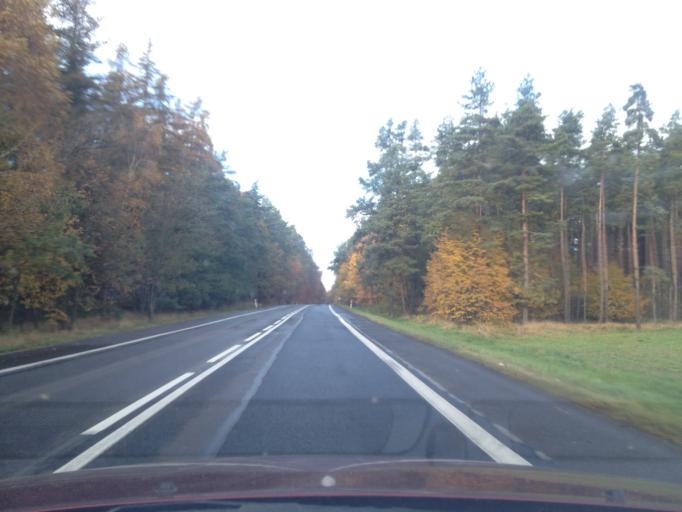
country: PL
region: Lower Silesian Voivodeship
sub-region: Powiat lubanski
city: Siekierczyn
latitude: 51.1555
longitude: 15.1555
